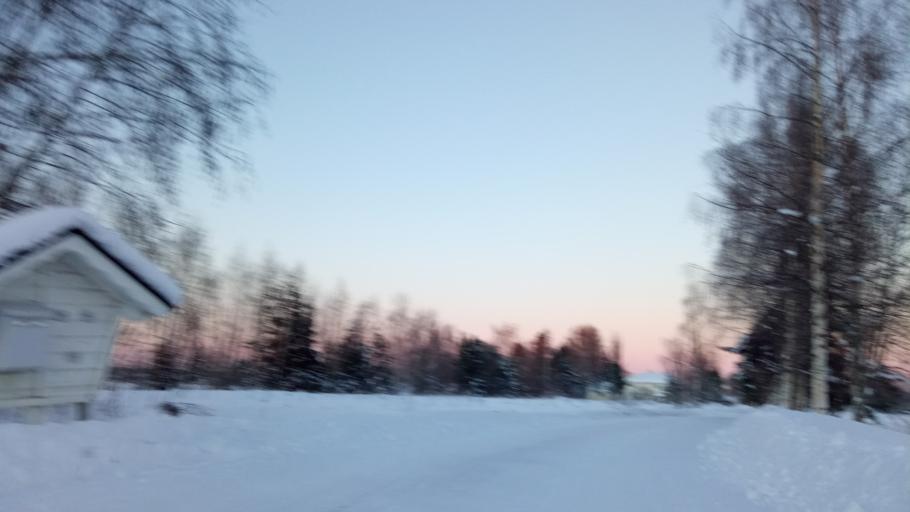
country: FI
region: Southern Ostrobothnia
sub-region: Jaerviseutu
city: Alajaervi
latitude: 62.9907
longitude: 23.8540
